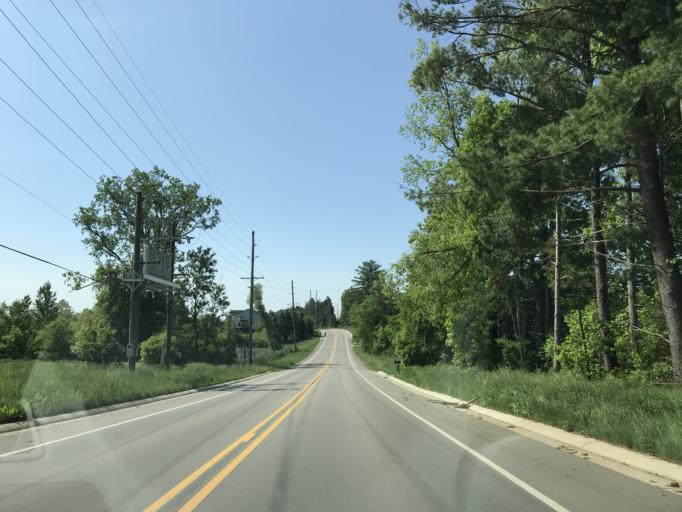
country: US
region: Michigan
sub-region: Oakland County
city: South Lyon
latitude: 42.4801
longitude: -83.6977
